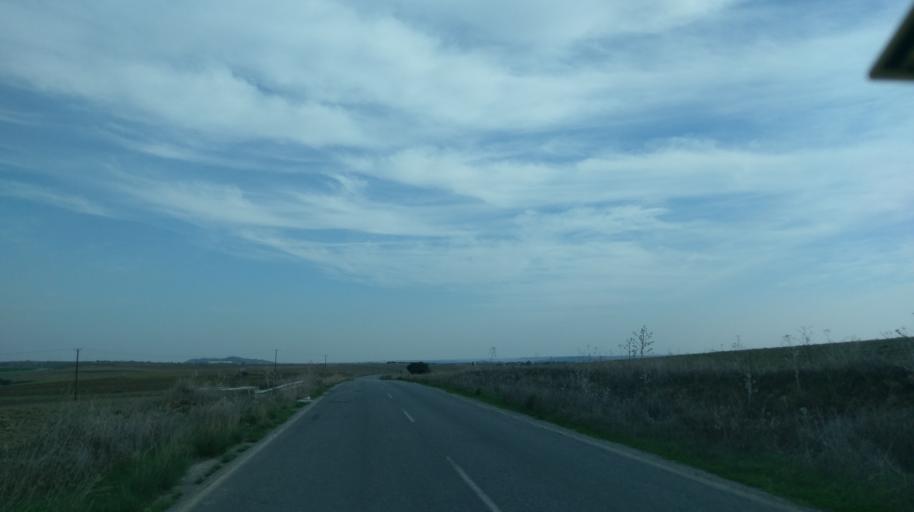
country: CY
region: Keryneia
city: Lapithos
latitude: 35.2510
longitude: 33.1477
